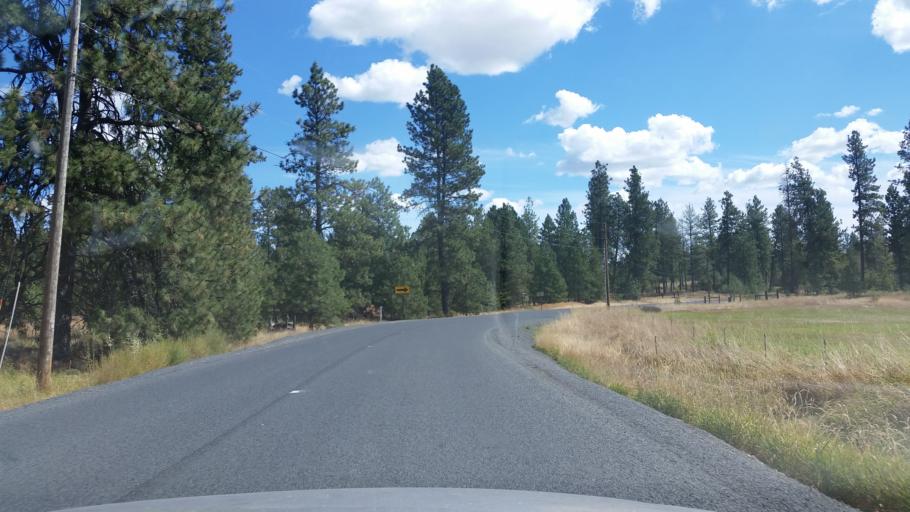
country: US
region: Washington
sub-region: Spokane County
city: Medical Lake
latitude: 47.5038
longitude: -117.6685
